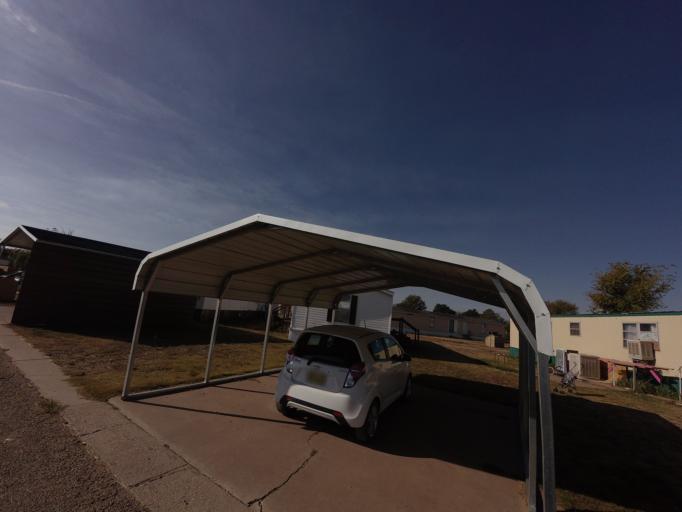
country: US
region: New Mexico
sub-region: Curry County
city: Clovis
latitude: 34.4096
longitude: -103.1742
